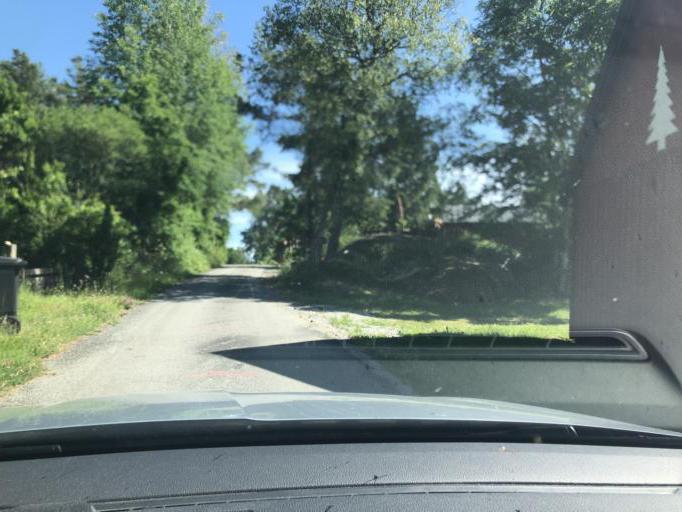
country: SE
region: Blekinge
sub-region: Karlshamns Kommun
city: Morrum
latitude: 56.1814
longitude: 14.7020
